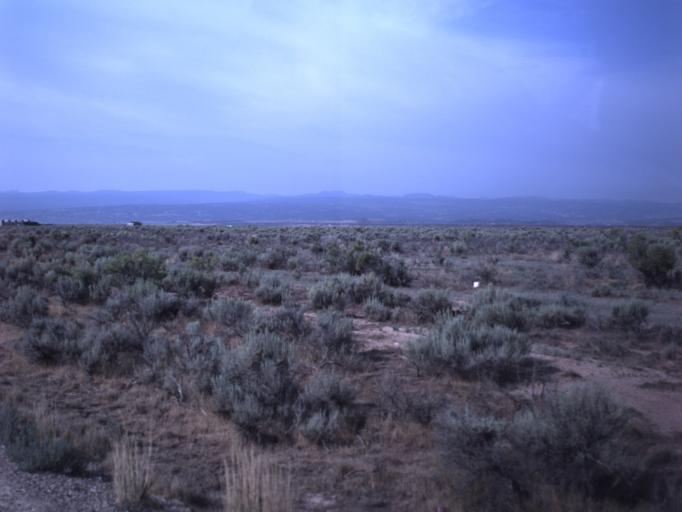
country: US
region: Utah
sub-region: Duchesne County
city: Duchesne
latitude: 40.2333
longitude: -110.3893
